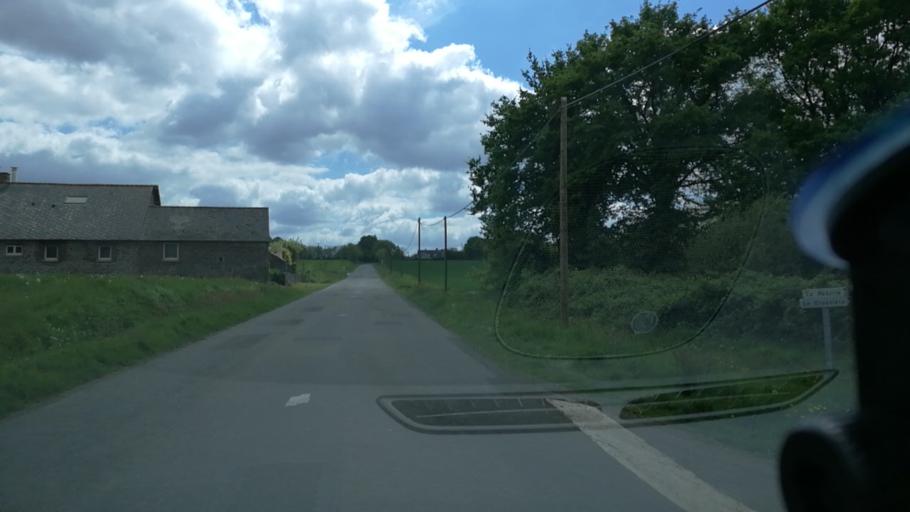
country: FR
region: Brittany
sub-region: Departement d'Ille-et-Vilaine
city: Retiers
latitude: 47.8968
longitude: -1.3828
